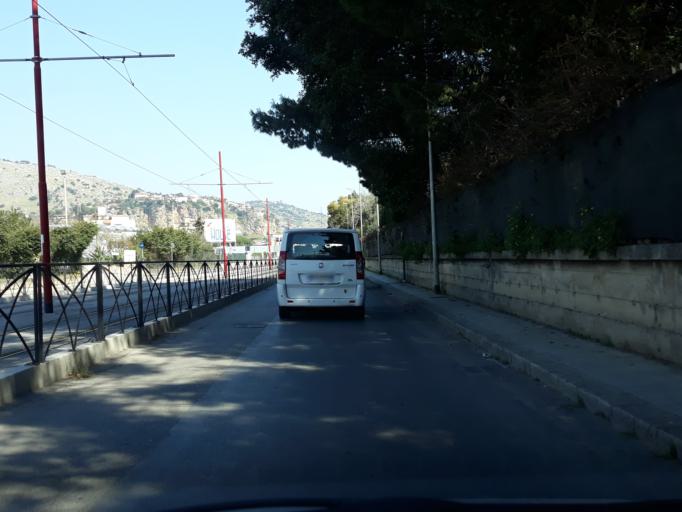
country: IT
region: Sicily
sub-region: Palermo
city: Palermo
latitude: 38.1269
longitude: 13.3026
